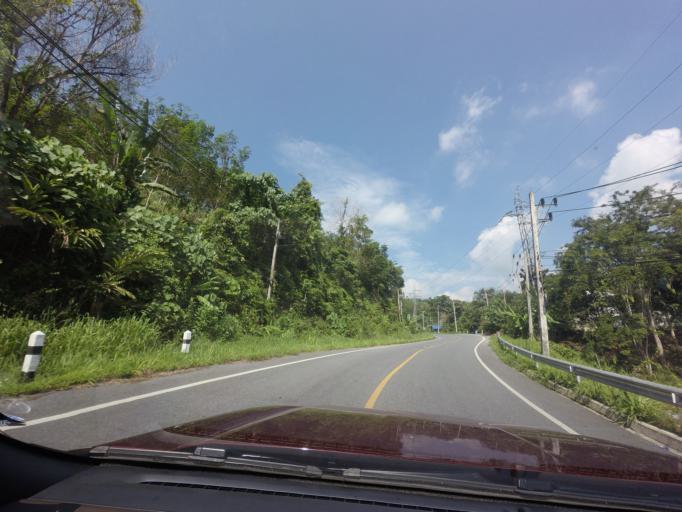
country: TH
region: Yala
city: Betong
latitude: 5.8815
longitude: 101.1399
